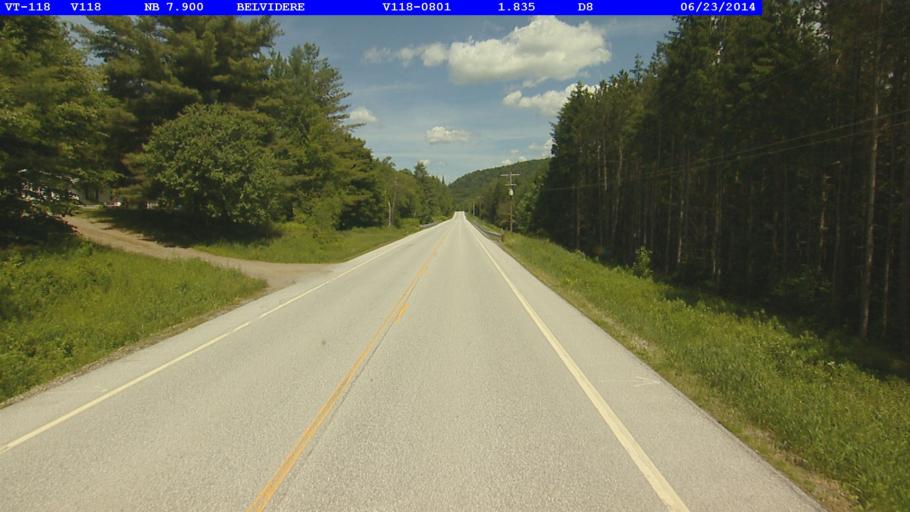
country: US
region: Vermont
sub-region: Lamoille County
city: Johnson
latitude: 44.7858
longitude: -72.6194
